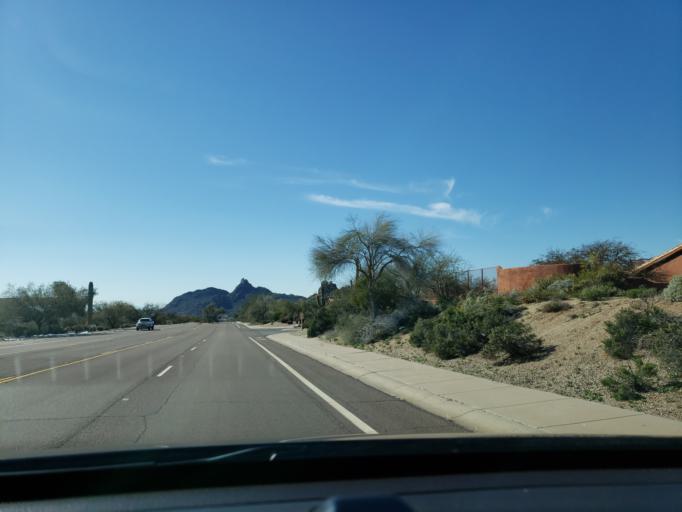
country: US
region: Arizona
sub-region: Maricopa County
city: Carefree
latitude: 33.7269
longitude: -111.8327
